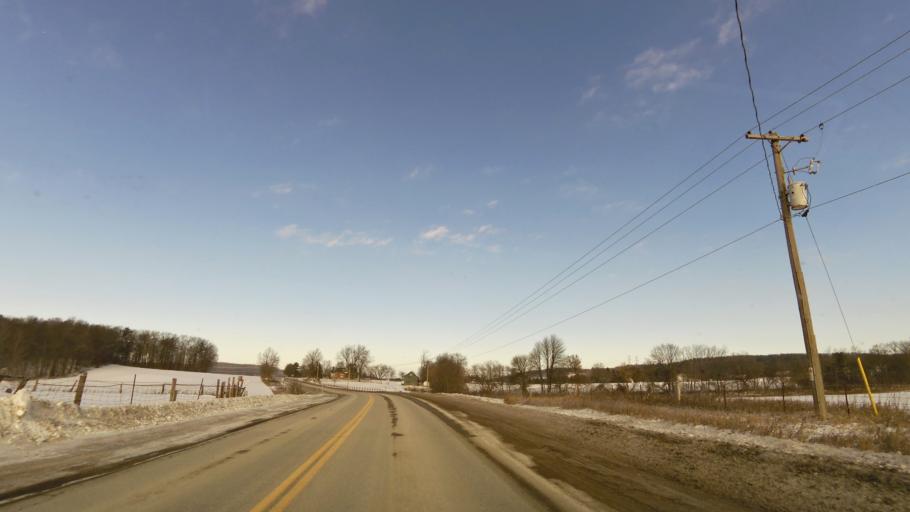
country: CA
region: Ontario
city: Quinte West
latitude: 44.1412
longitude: -77.7896
